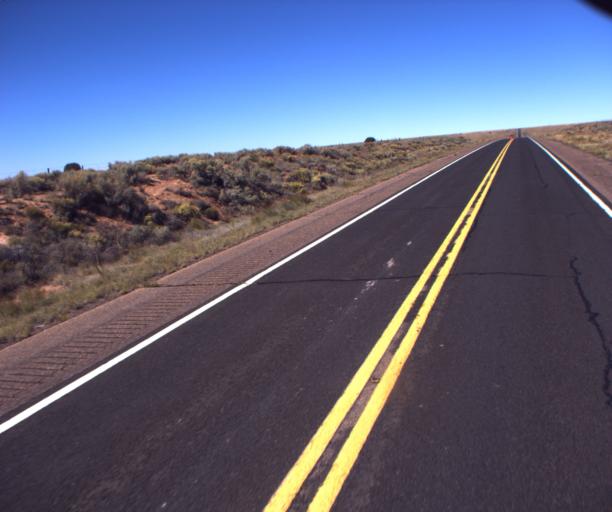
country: US
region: Arizona
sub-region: Navajo County
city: Snowflake
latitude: 34.6881
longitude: -109.7414
